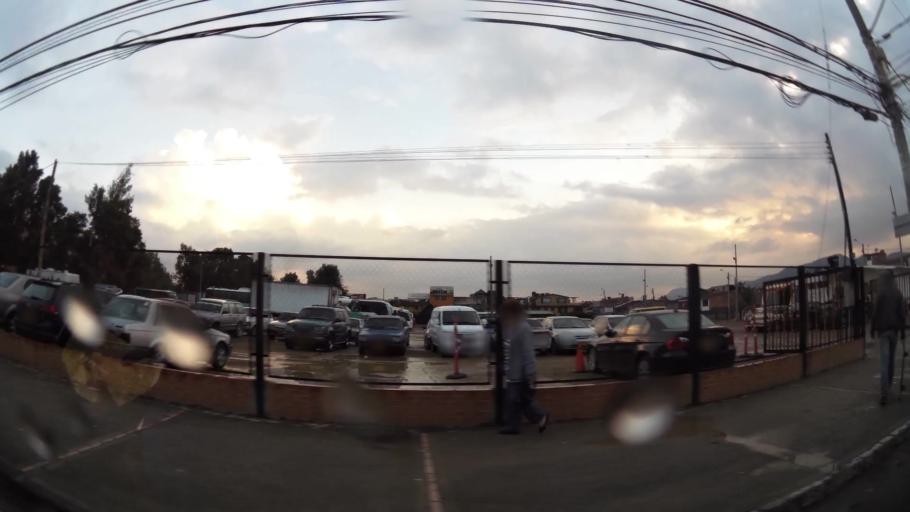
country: CO
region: Cundinamarca
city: Chia
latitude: 4.8564
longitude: -74.0580
